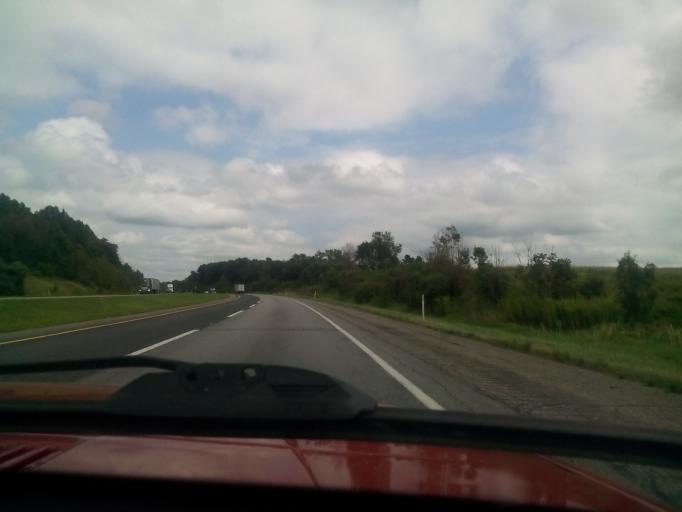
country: US
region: Indiana
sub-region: LaPorte County
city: Westville
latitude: 41.5955
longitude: -86.8707
